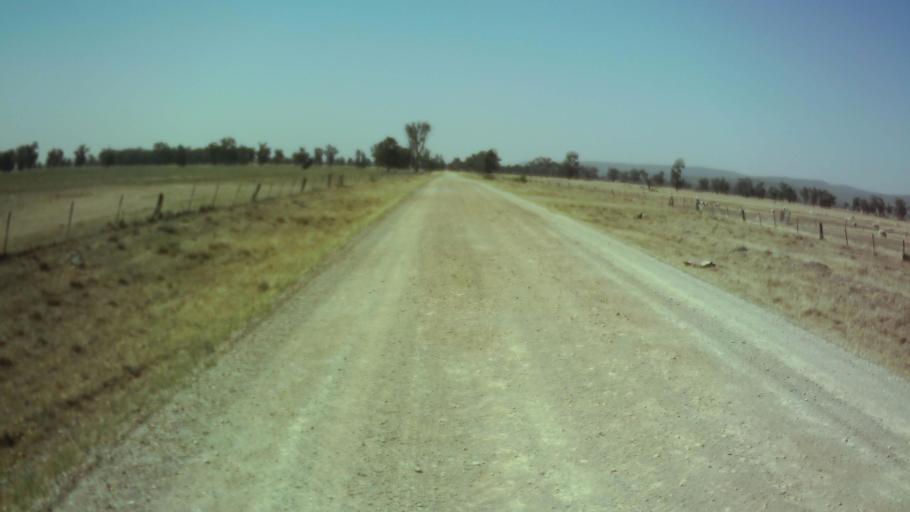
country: AU
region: New South Wales
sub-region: Weddin
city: Grenfell
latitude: -34.0284
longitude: 147.9130
